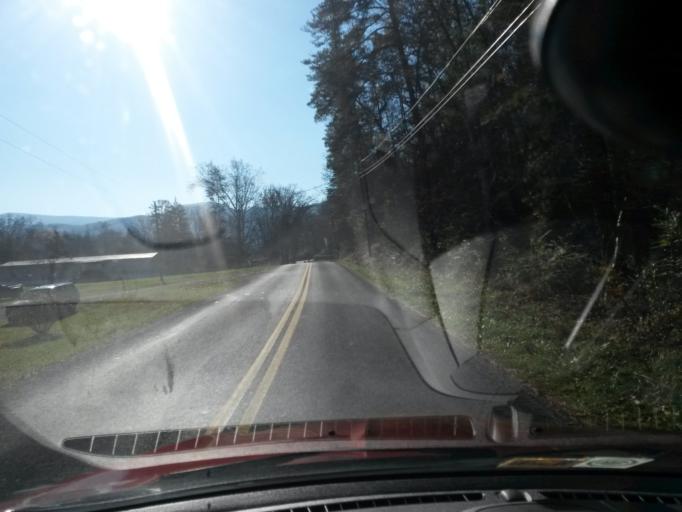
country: US
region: Virginia
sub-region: Alleghany County
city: Clifton Forge
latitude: 37.8067
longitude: -79.7441
